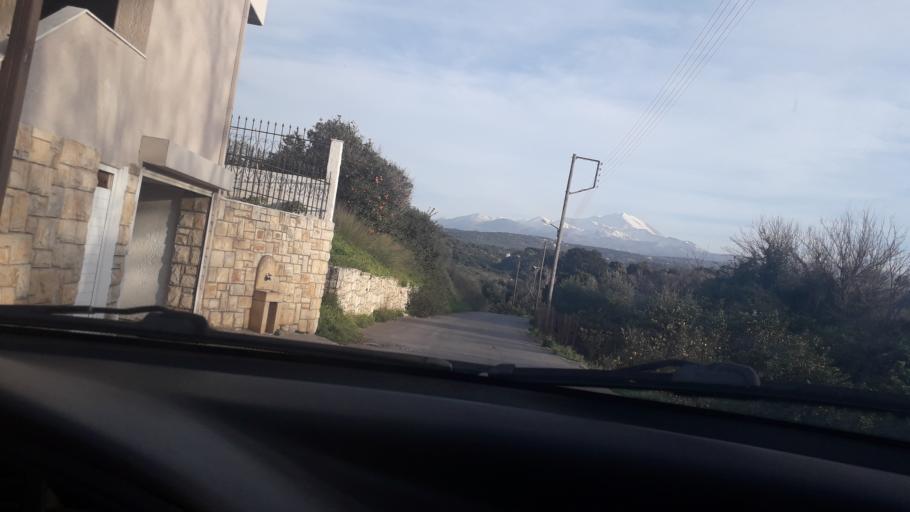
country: GR
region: Crete
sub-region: Nomos Rethymnis
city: Panormos
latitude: 35.3821
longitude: 24.6203
